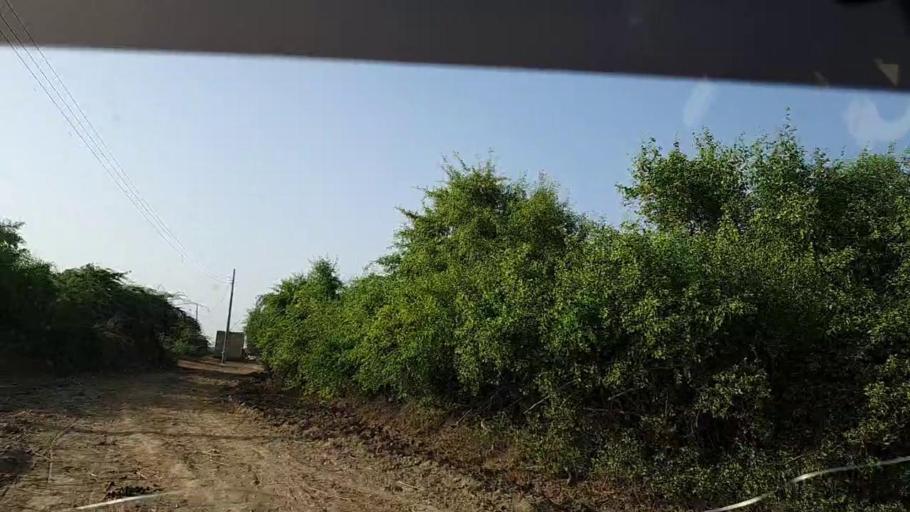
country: PK
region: Sindh
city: Badin
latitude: 24.5754
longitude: 68.8741
